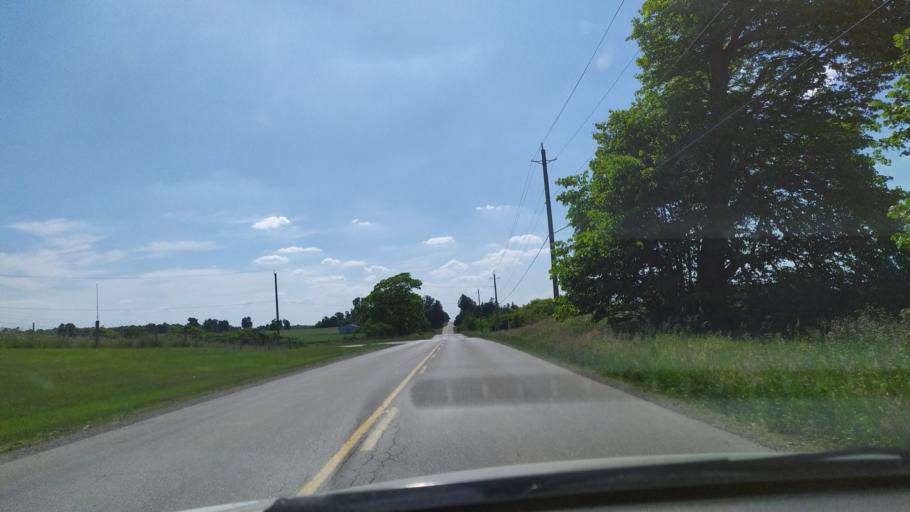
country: CA
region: Ontario
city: Kitchener
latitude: 43.3678
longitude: -80.5807
